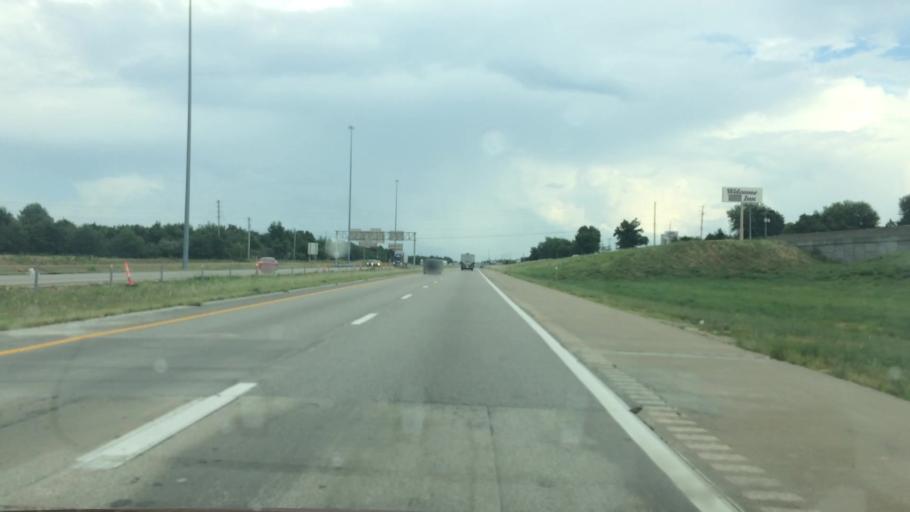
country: US
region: Missouri
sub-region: Greene County
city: Springfield
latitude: 37.2501
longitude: -93.2228
